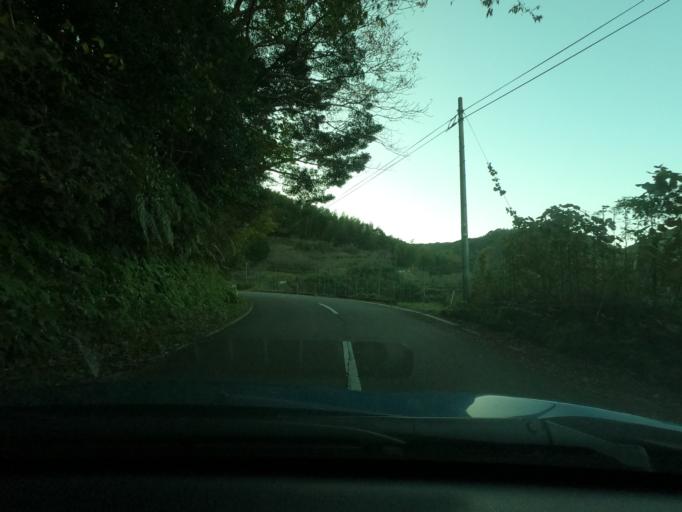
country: JP
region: Kagoshima
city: Satsumasendai
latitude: 31.8215
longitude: 130.4816
